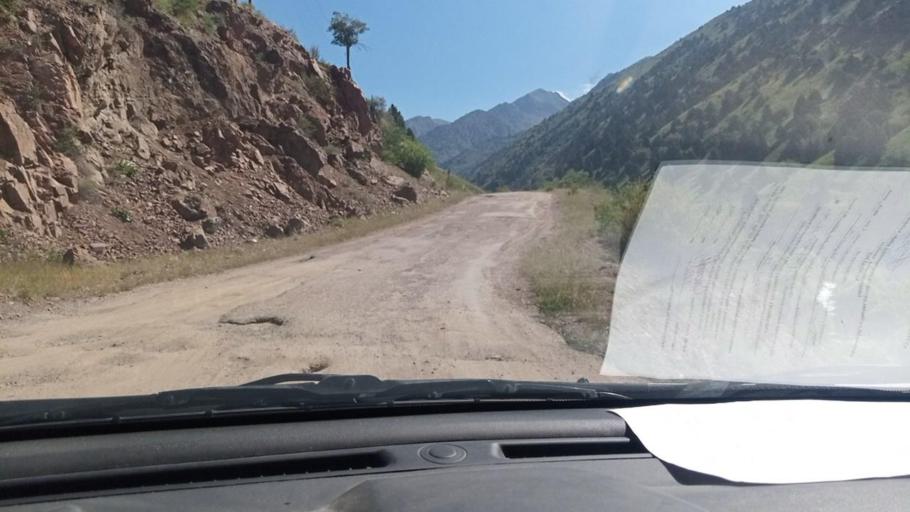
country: UZ
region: Toshkent
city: Yangiobod
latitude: 41.1297
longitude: 70.1110
